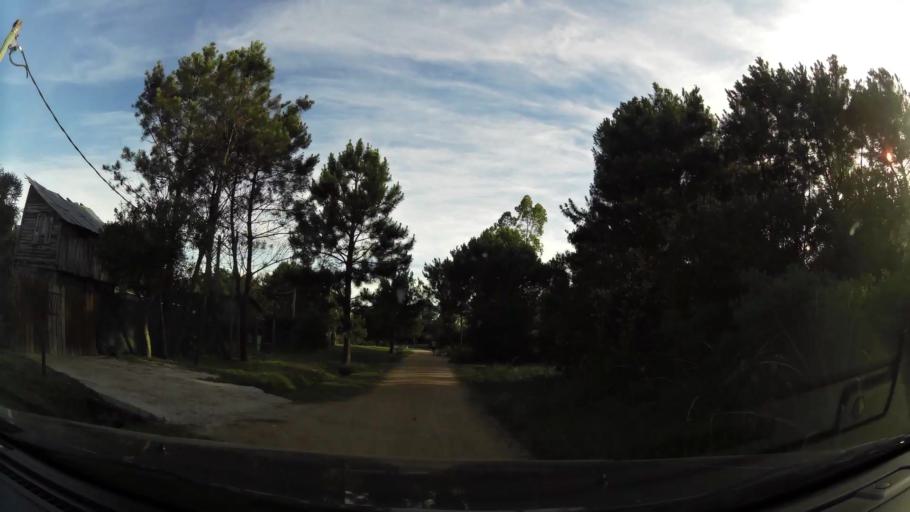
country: UY
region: Canelones
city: Empalme Olmos
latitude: -34.7693
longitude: -55.8641
